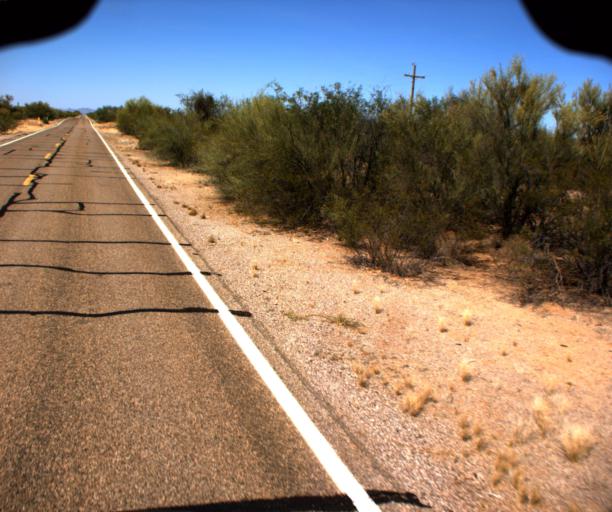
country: US
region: Arizona
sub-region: Pima County
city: Three Points
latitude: 31.9926
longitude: -111.3673
